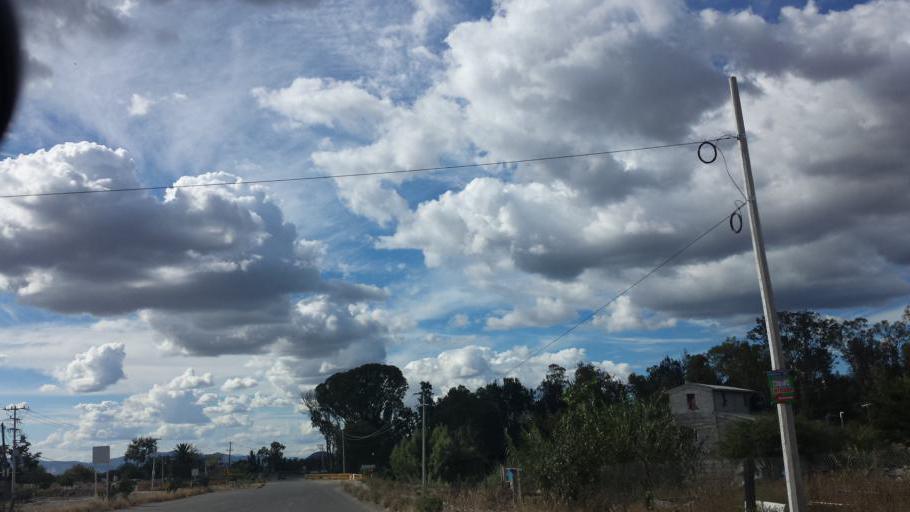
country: MX
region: Oaxaca
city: Tlacolula de Matamoros
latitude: 16.9506
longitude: -96.4646
